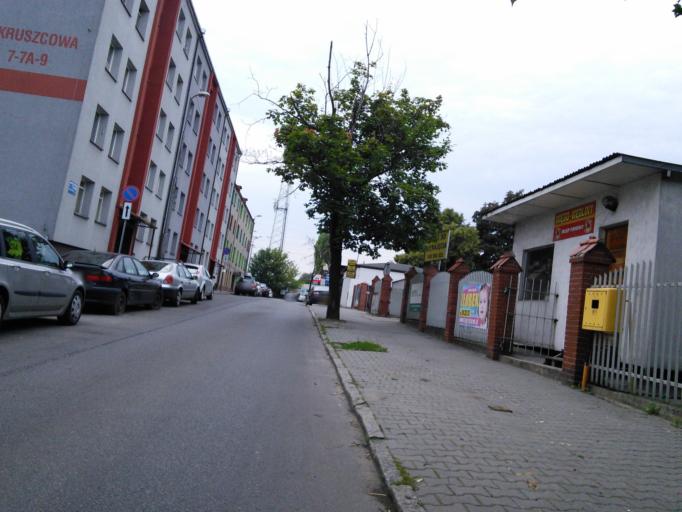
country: PL
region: Silesian Voivodeship
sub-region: Bytom
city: Bytom
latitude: 50.3598
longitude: 18.9327
